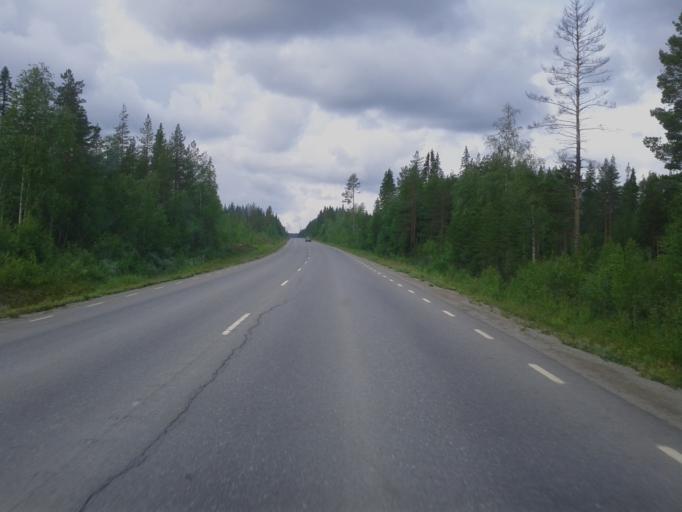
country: SE
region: Vaesterbotten
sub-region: Norsjo Kommun
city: Norsjoe
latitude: 64.9872
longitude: 19.4612
